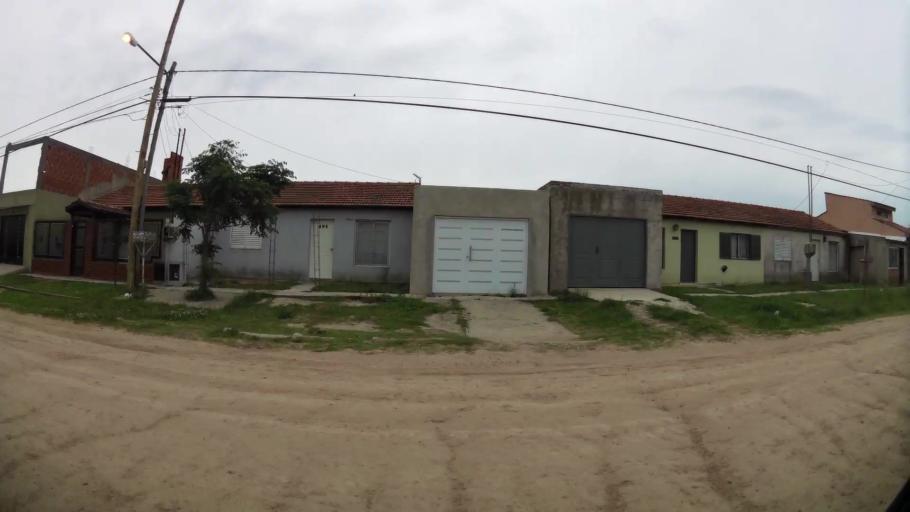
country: AR
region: Buenos Aires
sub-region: Partido de Campana
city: Campana
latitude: -34.2057
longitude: -58.9480
